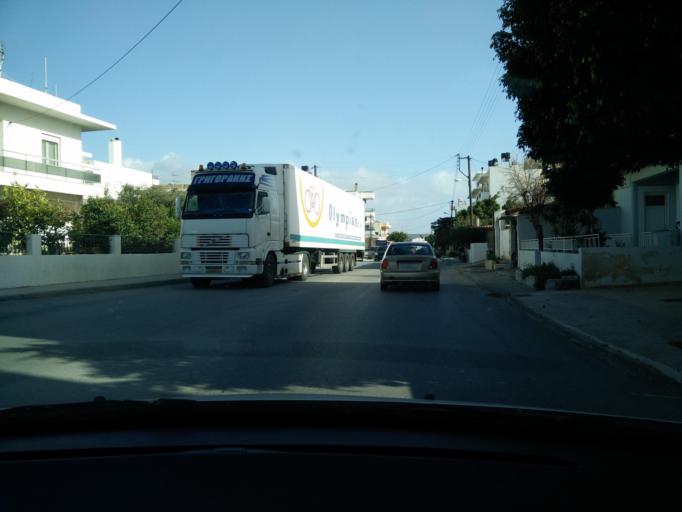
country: GR
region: Crete
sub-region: Nomos Lasithiou
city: Ierapetra
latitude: 35.0152
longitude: 25.7371
